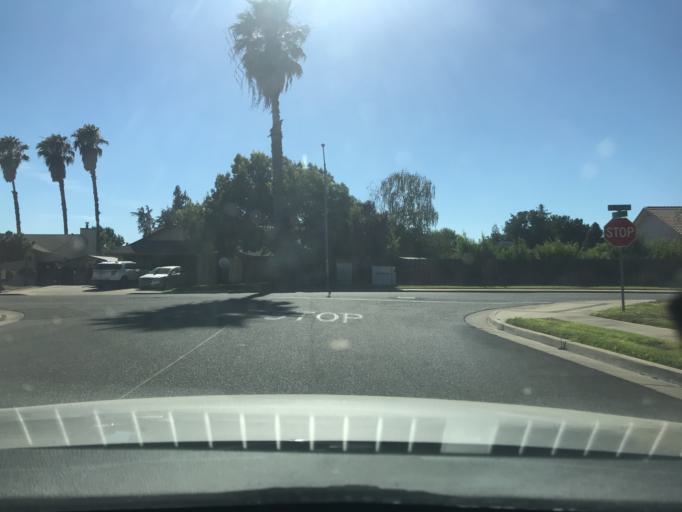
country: US
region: California
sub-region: Merced County
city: Atwater
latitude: 37.3486
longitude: -120.5865
